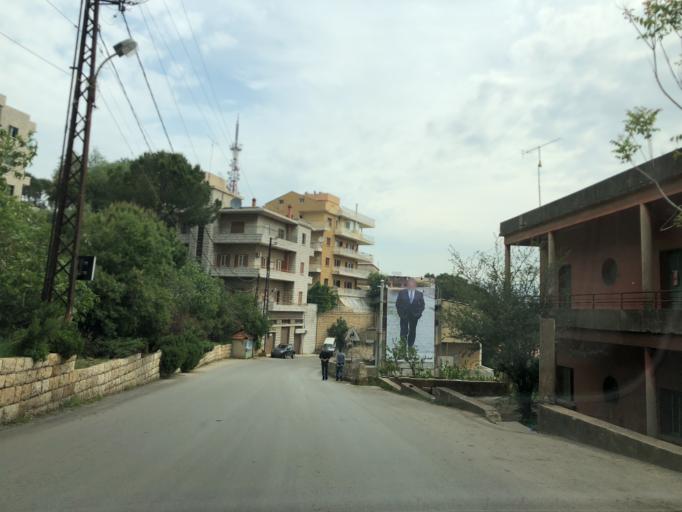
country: LB
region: Mont-Liban
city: Jdaidet el Matn
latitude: 33.8698
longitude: 35.6086
